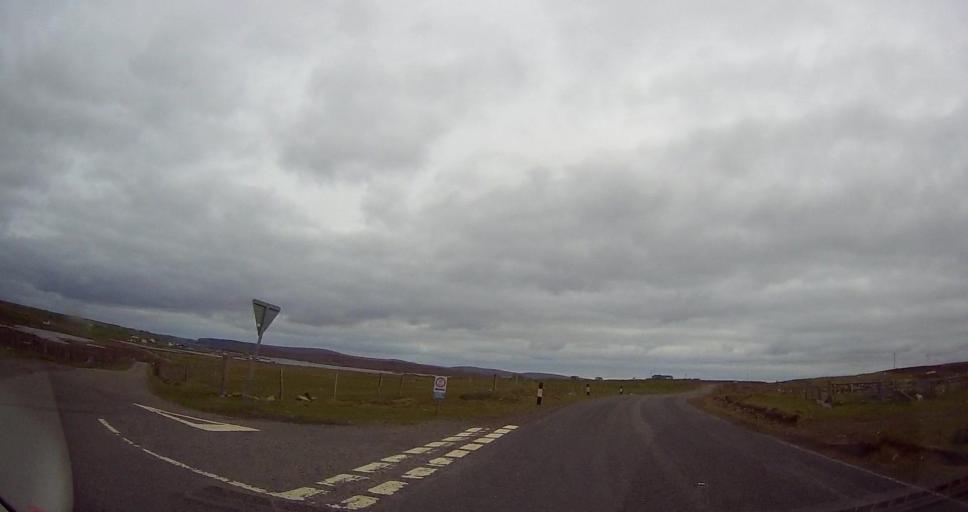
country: GB
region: Scotland
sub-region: Shetland Islands
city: Shetland
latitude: 60.7008
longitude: -0.9206
